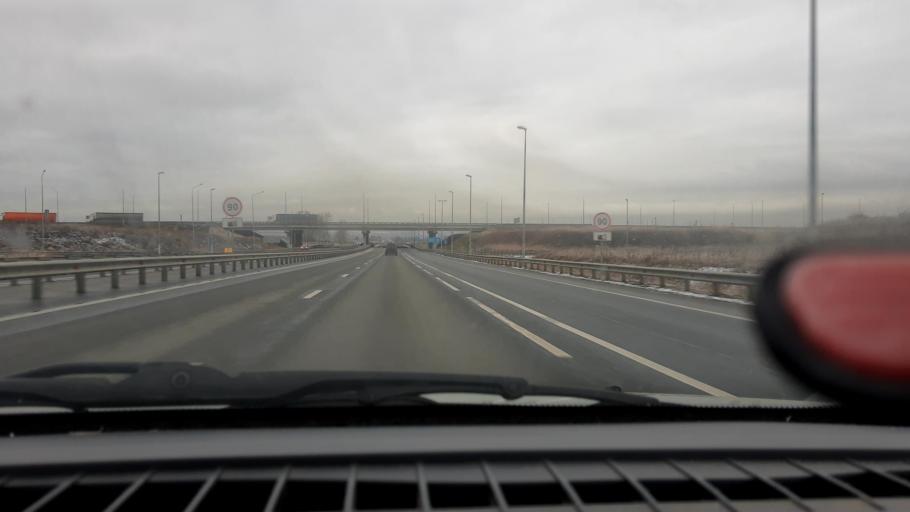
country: RU
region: Nizjnij Novgorod
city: Burevestnik
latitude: 56.1150
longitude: 43.9166
